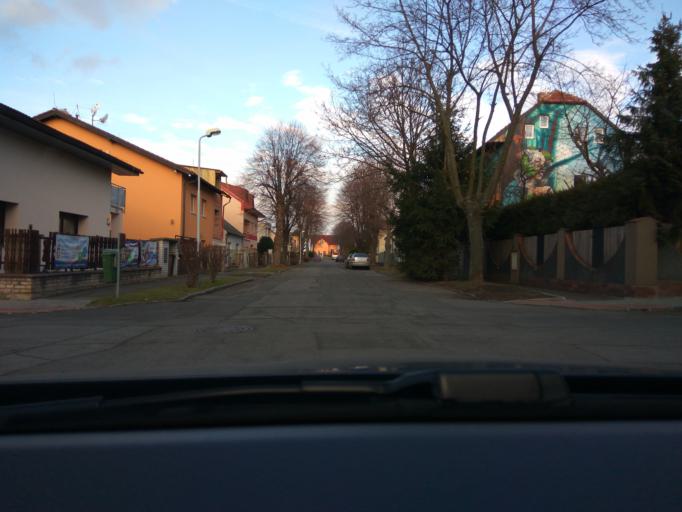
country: CZ
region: Praha
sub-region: Praha 18
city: Letnany
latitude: 50.1535
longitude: 14.5304
